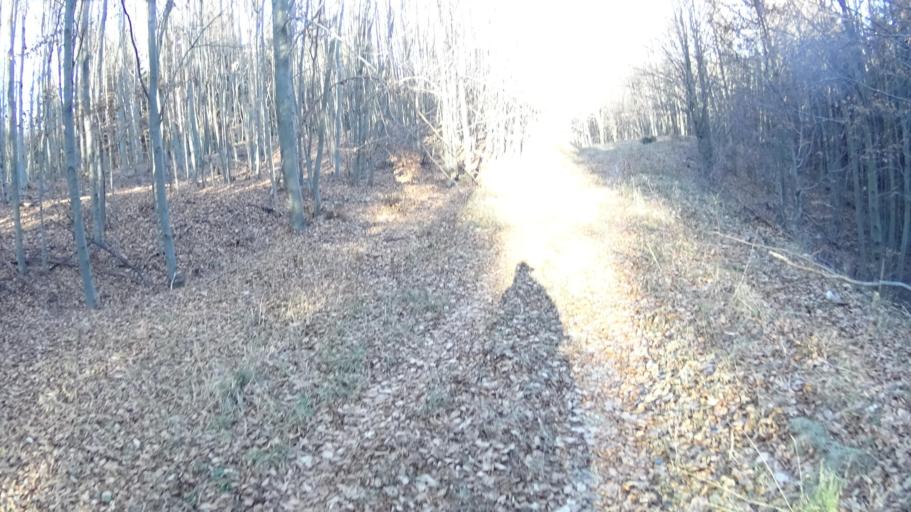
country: HU
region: Heves
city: Szilvasvarad
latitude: 48.0779
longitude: 20.4769
